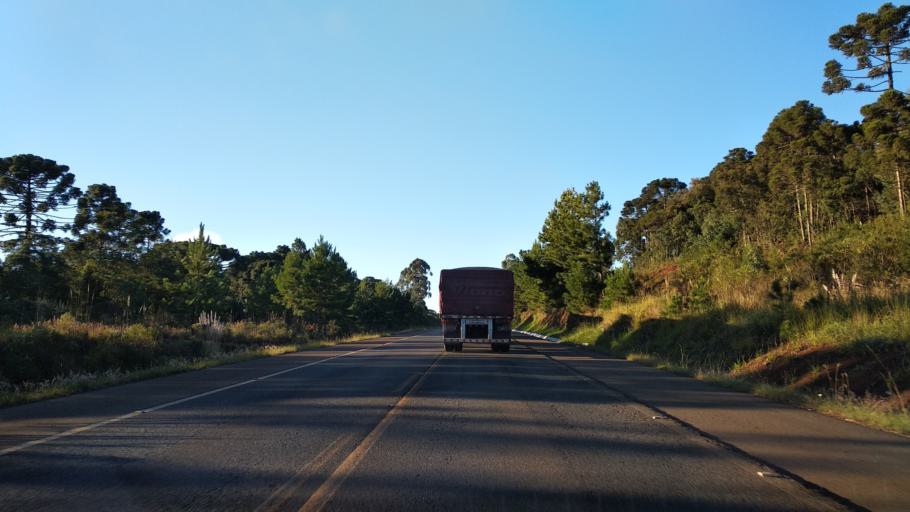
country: BR
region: Santa Catarina
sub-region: Correia Pinto
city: Correia Pinto
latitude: -27.6394
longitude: -50.5975
